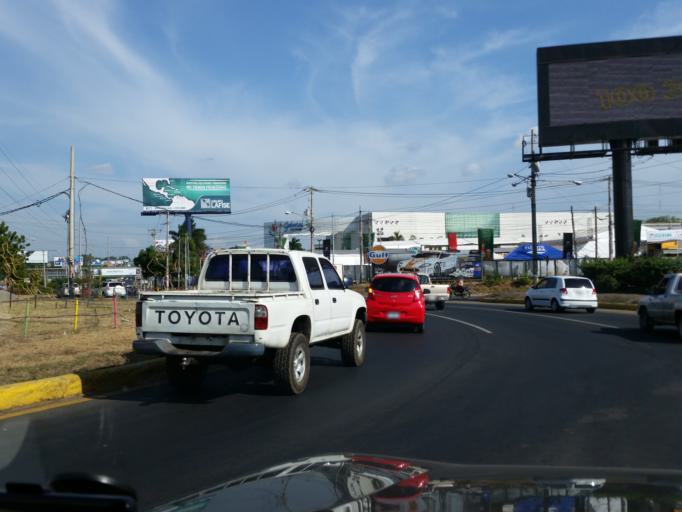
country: NI
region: Managua
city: Managua
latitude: 12.1064
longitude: -86.2492
